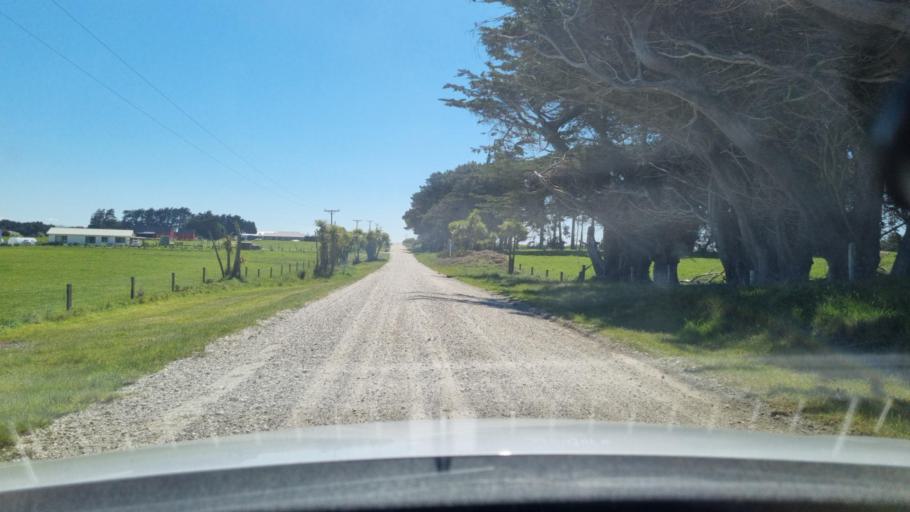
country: NZ
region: Southland
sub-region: Invercargill City
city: Invercargill
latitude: -46.4147
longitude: 168.2634
